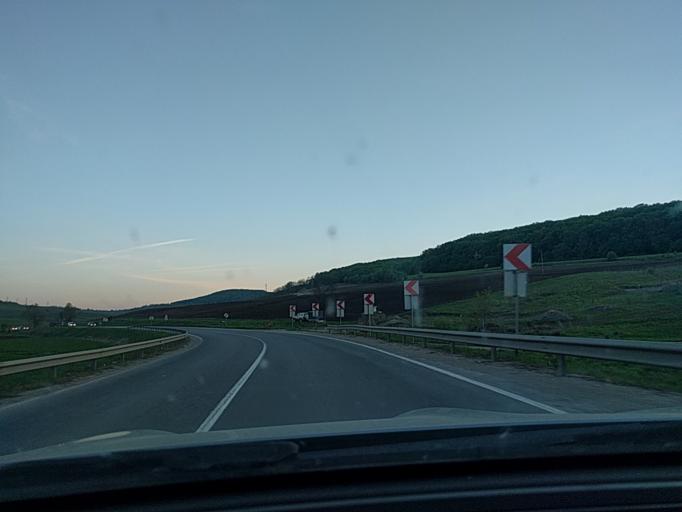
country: RO
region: Mures
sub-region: Comuna Nades
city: Nades
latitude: 46.3165
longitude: 24.7218
